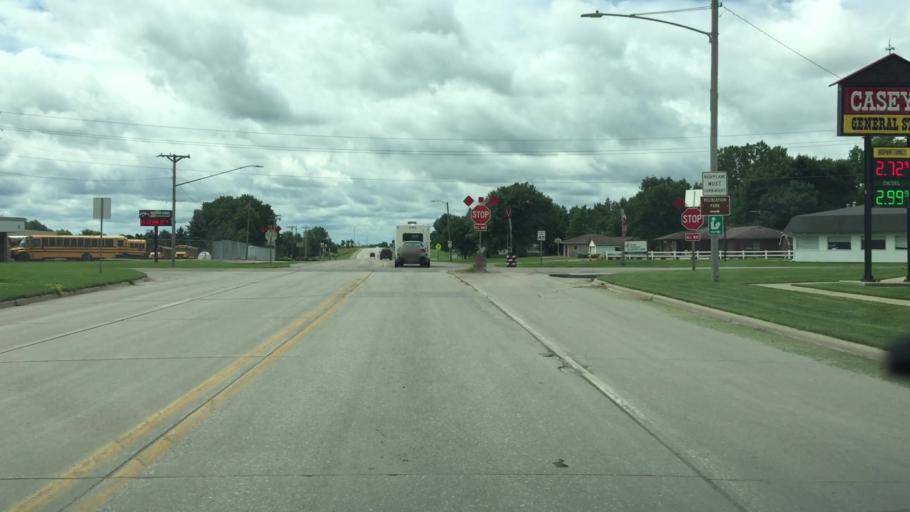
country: US
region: Iowa
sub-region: Jasper County
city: Monroe
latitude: 41.5176
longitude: -93.1018
